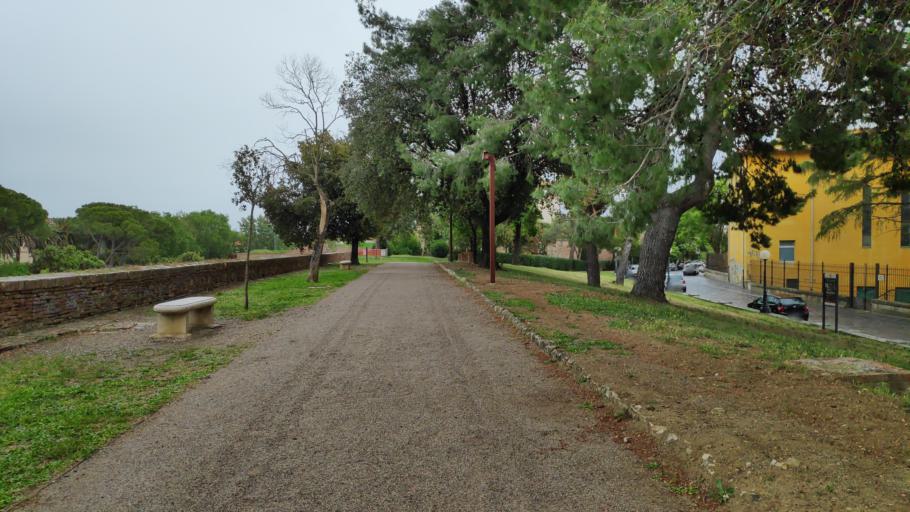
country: IT
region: Tuscany
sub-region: Provincia di Grosseto
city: Grosseto
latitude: 42.7626
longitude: 11.1151
